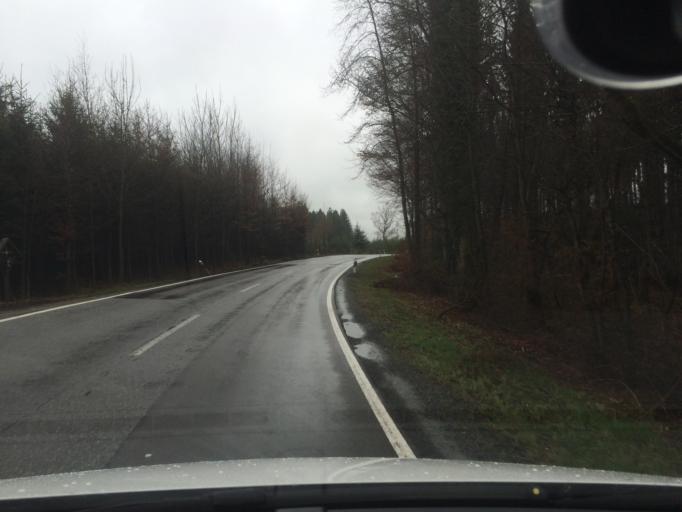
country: DE
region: Bavaria
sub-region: Upper Bavaria
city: Tuntenhausen
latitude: 47.9462
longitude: 11.9761
